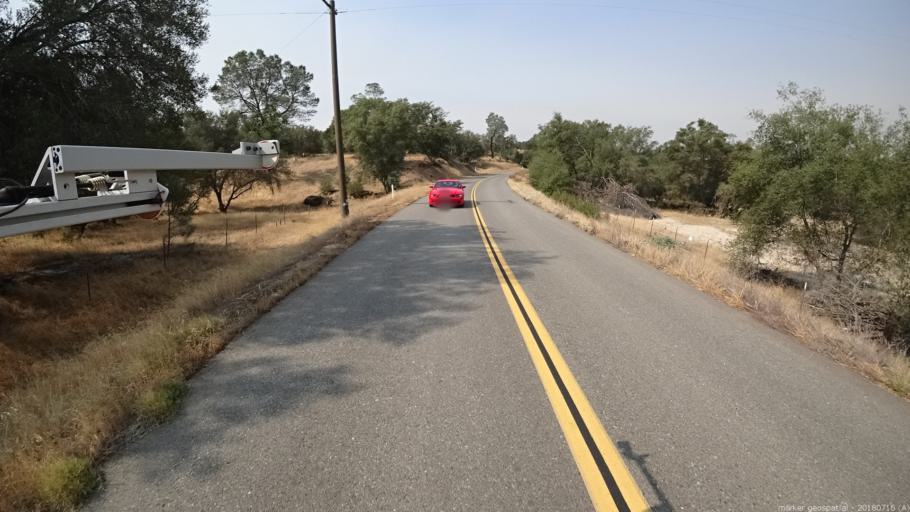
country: US
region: California
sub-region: Madera County
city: Yosemite Lakes
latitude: 37.1680
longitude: -119.8355
